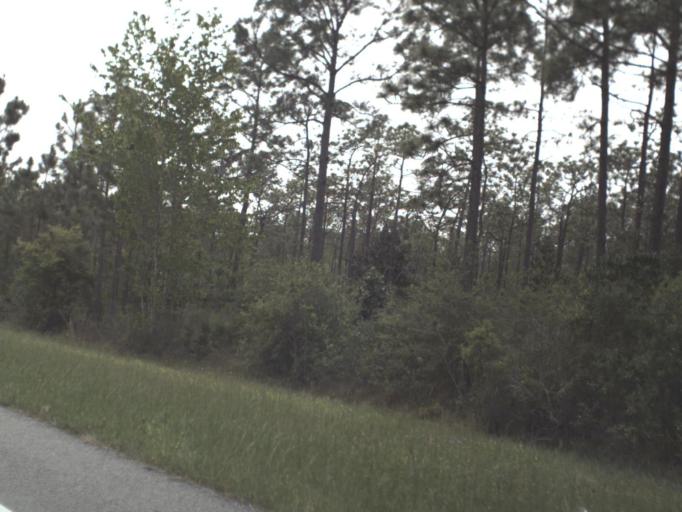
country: US
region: Florida
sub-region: Escambia County
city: Myrtle Grove
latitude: 30.3676
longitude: -87.3600
